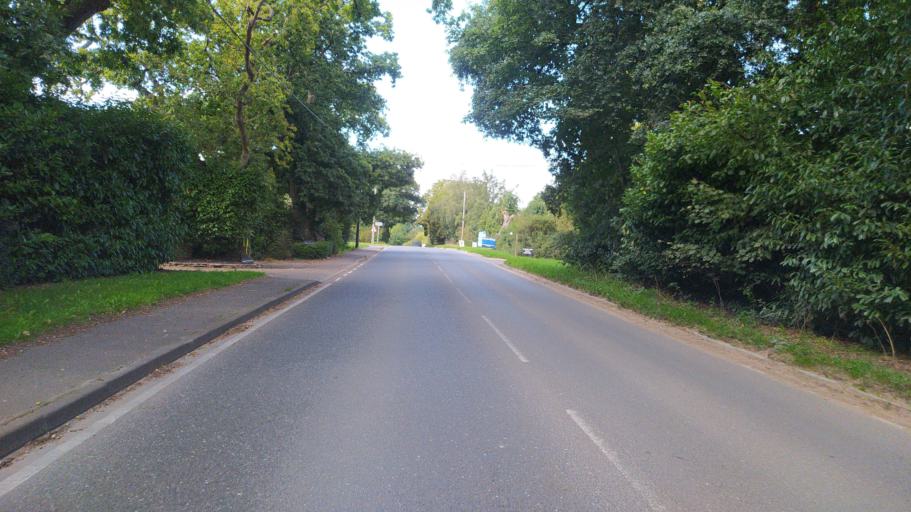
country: GB
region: England
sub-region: Hampshire
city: Romsey
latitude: 51.0118
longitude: -1.4917
